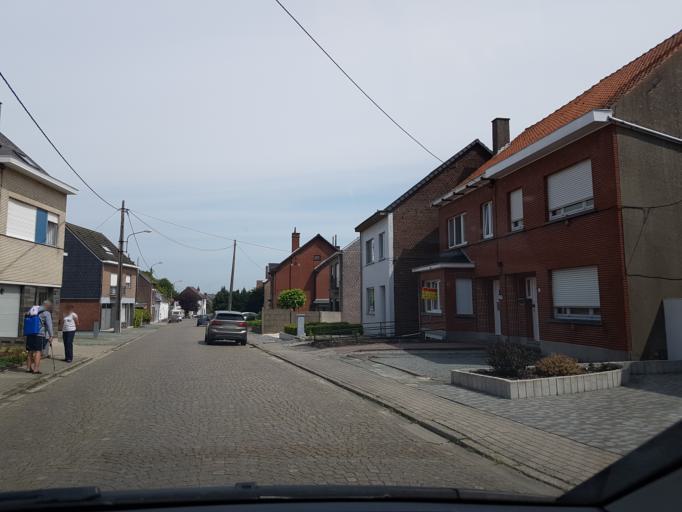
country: BE
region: Flanders
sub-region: Provincie Oost-Vlaanderen
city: Denderleeuw
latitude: 50.9148
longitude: 4.1044
